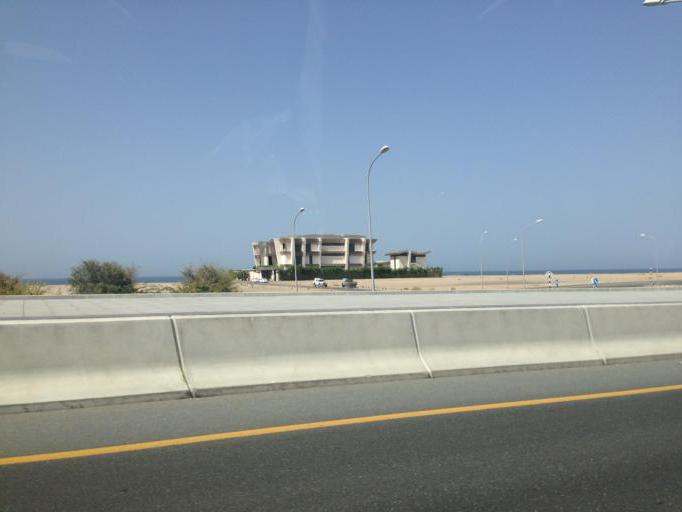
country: OM
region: Muhafazat Masqat
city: Bawshar
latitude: 23.6078
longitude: 58.3142
